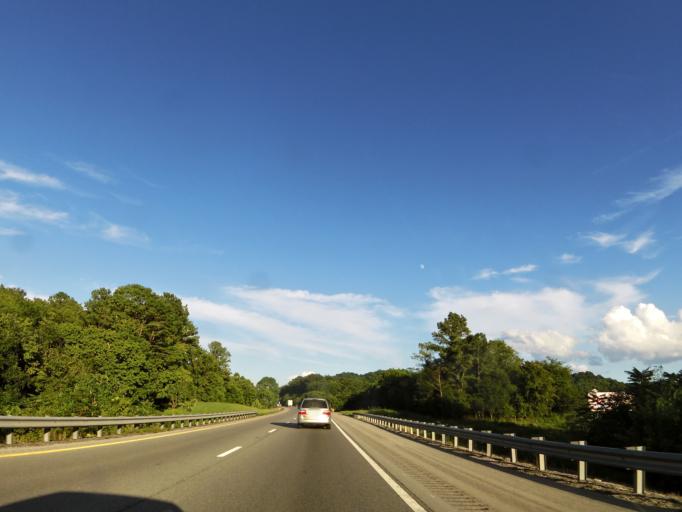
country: US
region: Tennessee
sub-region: Smith County
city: Gordonsville
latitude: 36.1429
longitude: -85.8454
